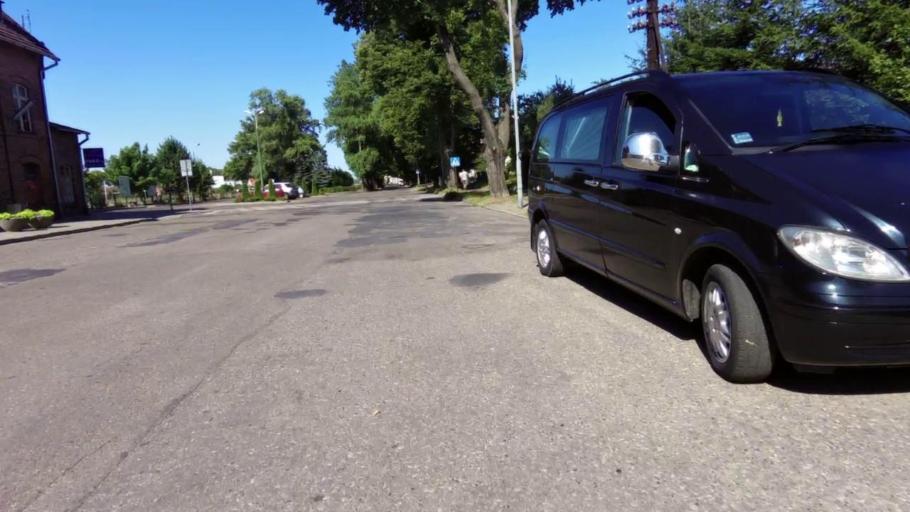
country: PL
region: West Pomeranian Voivodeship
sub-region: Powiat drawski
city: Zlocieniec
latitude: 53.5284
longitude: 16.0186
